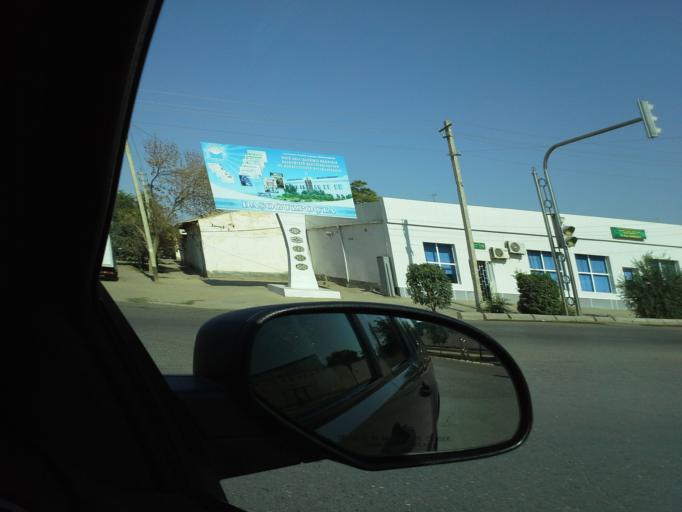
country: TM
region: Dasoguz
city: Dasoguz
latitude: 41.8233
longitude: 59.9770
